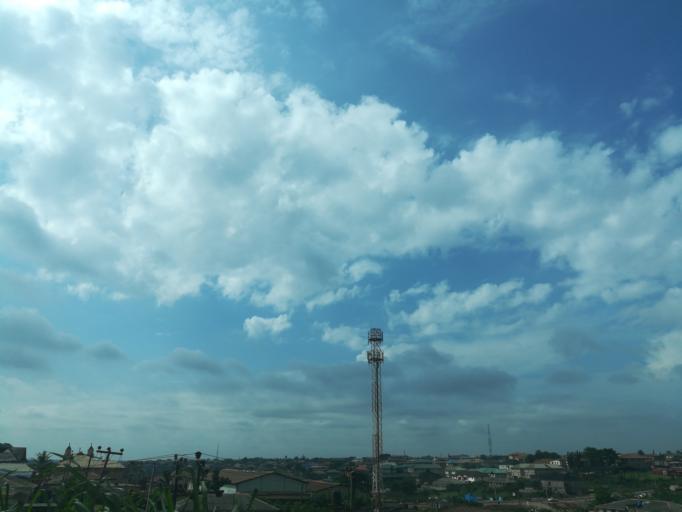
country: NG
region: Lagos
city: Ikorodu
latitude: 6.6321
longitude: 3.5323
